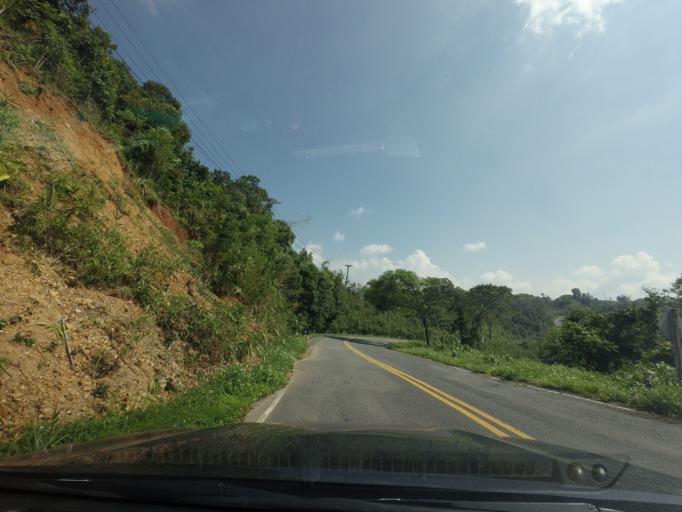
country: TH
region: Nan
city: Bo Kluea
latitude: 19.0520
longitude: 101.0904
